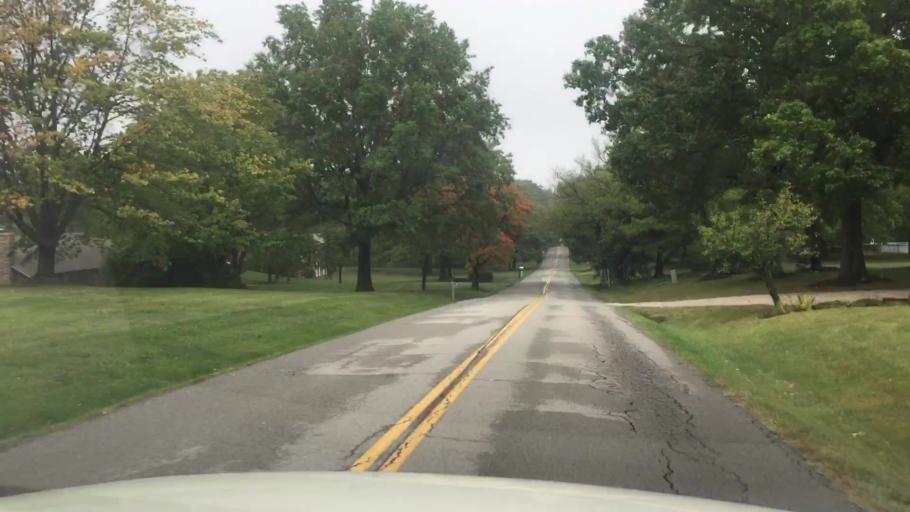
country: US
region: Missouri
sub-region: Boone County
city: Columbia
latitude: 38.8579
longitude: -92.3150
